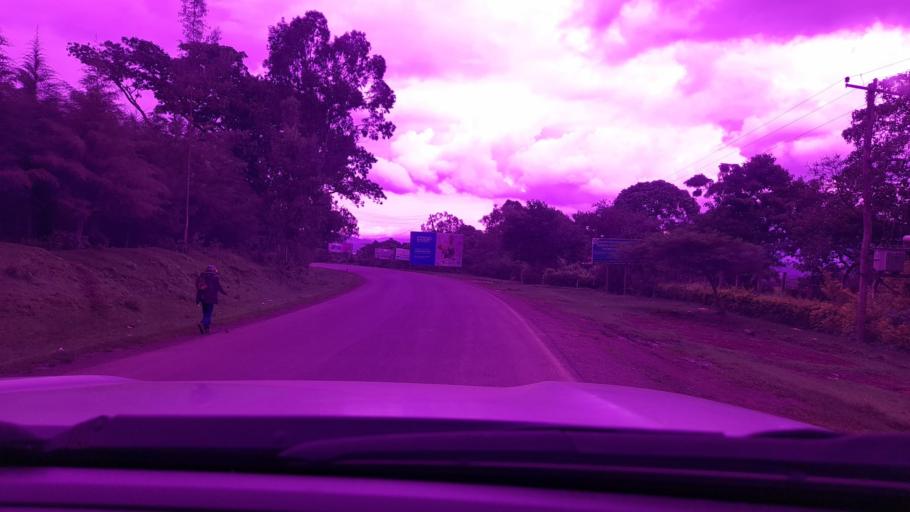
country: ET
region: Oromiya
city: Jima
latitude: 7.6652
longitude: 36.8724
